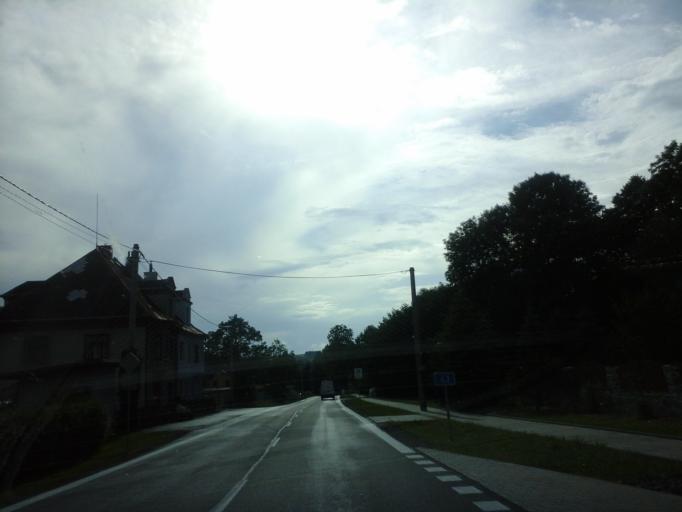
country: CZ
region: Olomoucky
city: Stity
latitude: 49.9607
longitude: 16.7188
